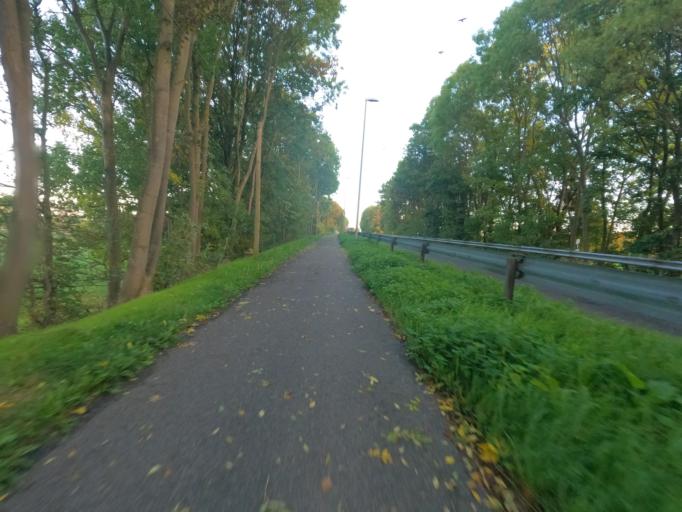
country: DE
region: North Rhine-Westphalia
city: Erkelenz
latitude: 51.0680
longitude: 6.3262
